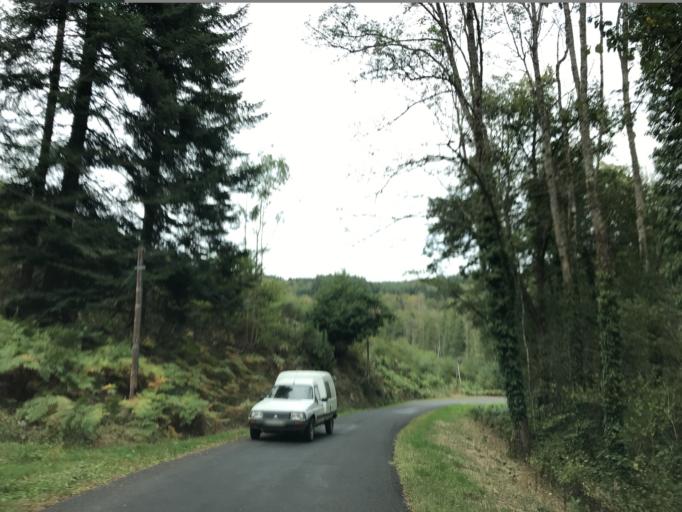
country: FR
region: Auvergne
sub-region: Departement du Puy-de-Dome
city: Escoutoux
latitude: 45.8269
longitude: 3.5986
